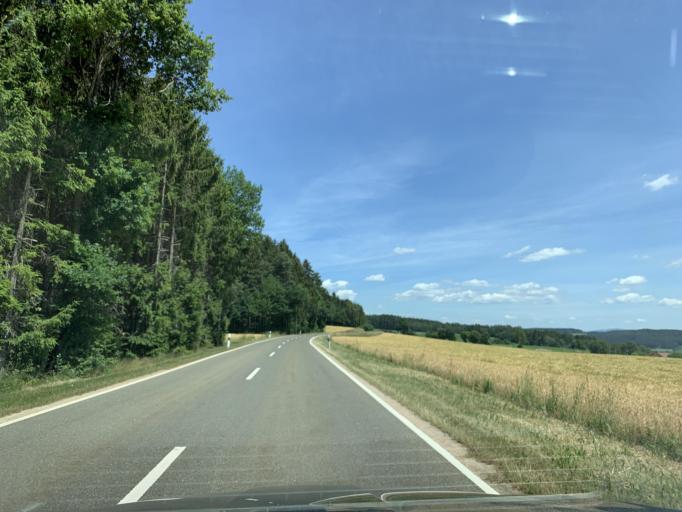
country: DE
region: Bavaria
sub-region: Upper Palatinate
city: Bach
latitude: 49.4184
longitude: 12.3898
